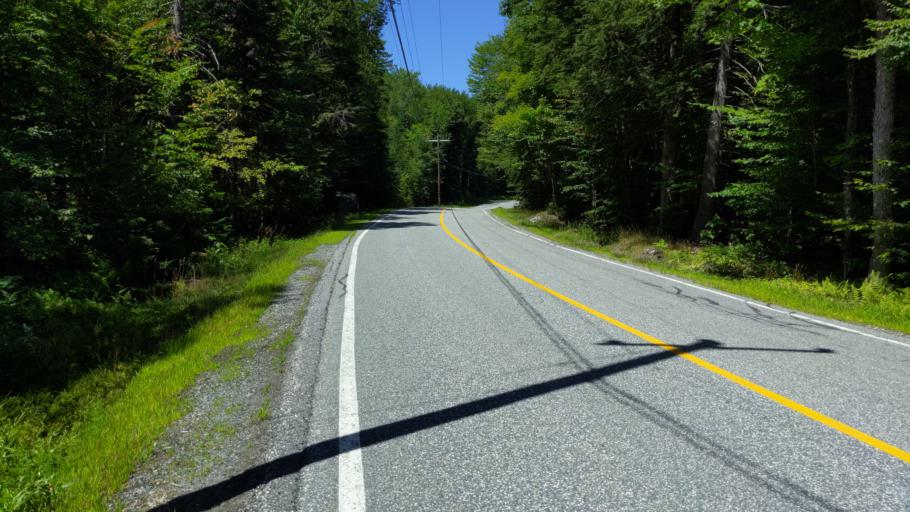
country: US
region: New Hampshire
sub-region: Sullivan County
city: Grantham
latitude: 43.5094
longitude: -72.1024
